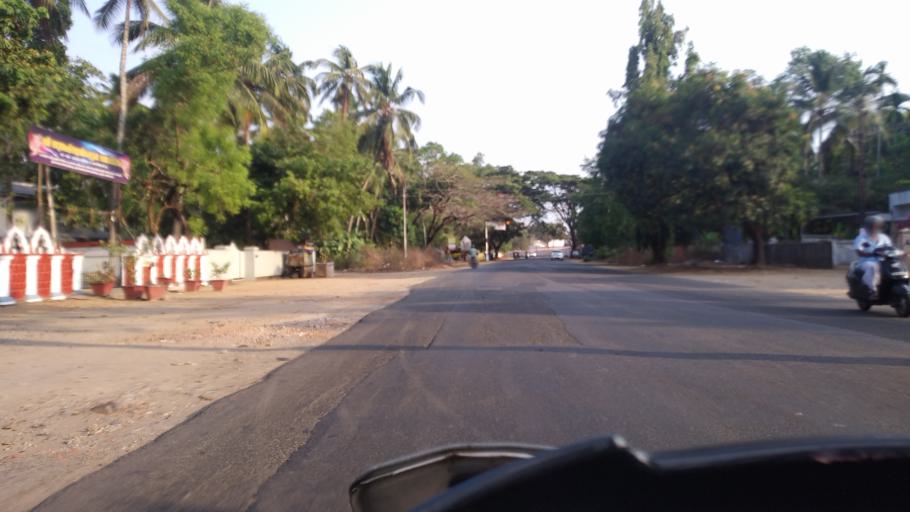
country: IN
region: Kerala
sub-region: Thrissur District
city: Thanniyam
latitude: 10.4298
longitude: 76.1003
